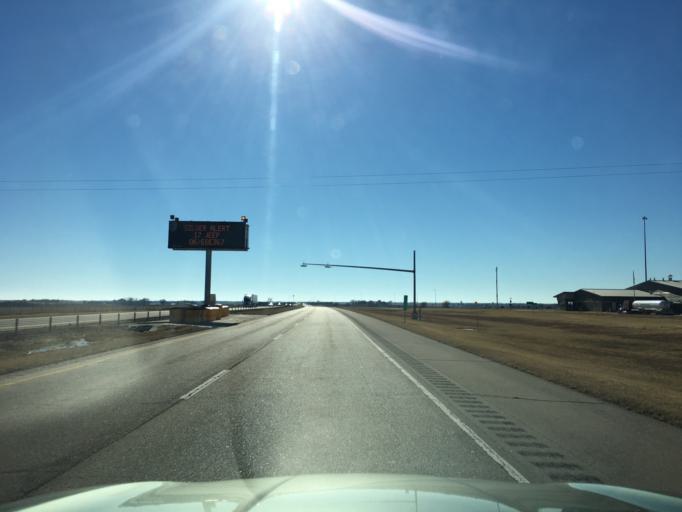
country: US
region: Oklahoma
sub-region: Kay County
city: Blackwell
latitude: 36.9856
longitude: -97.3456
